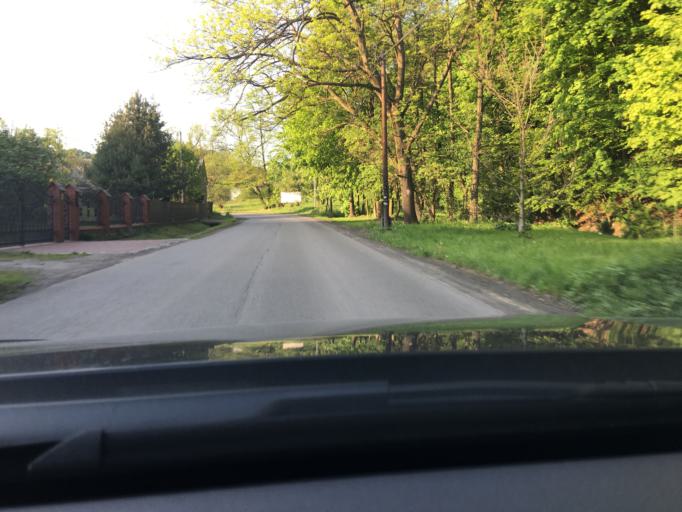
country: PL
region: Lesser Poland Voivodeship
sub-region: Powiat krakowski
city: Jerzmanowice
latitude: 50.1852
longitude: 19.7173
